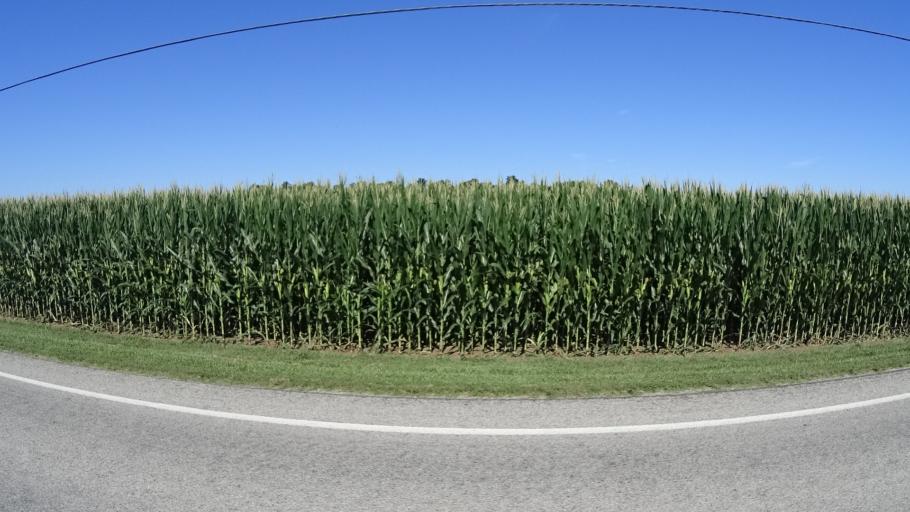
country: US
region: Ohio
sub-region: Erie County
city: Sandusky
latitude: 41.3770
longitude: -82.7240
